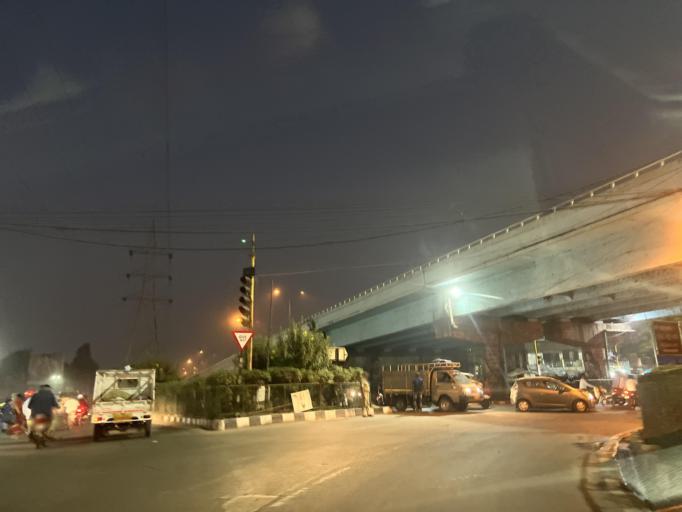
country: IN
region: Odisha
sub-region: Cuttack
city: Cuttack
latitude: 20.4567
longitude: 85.9012
